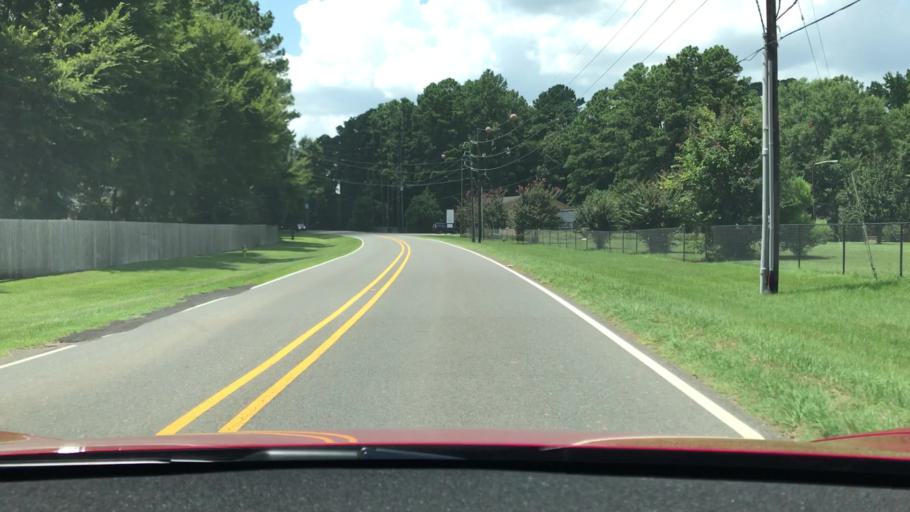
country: US
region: Louisiana
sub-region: De Soto Parish
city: Stonewall
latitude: 32.3685
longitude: -93.7025
